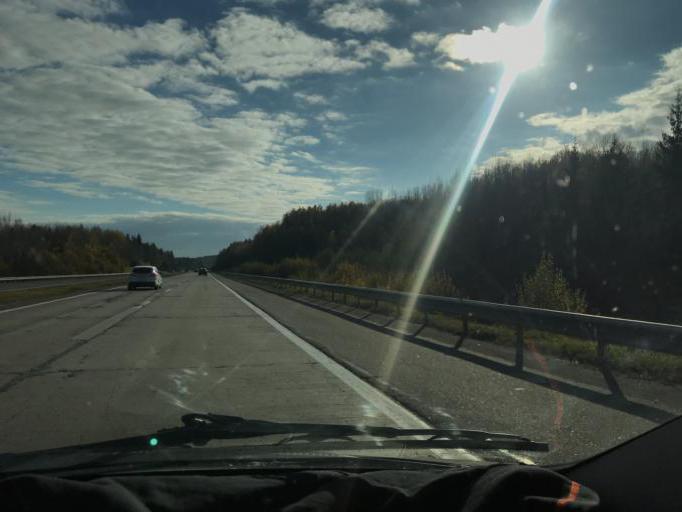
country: BY
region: Minsk
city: Lahoysk
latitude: 54.1292
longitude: 27.8079
